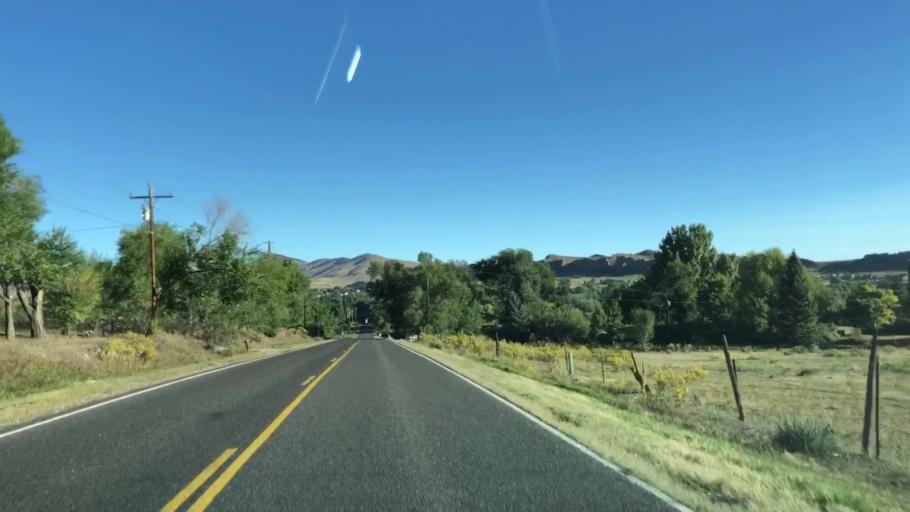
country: US
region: Colorado
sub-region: Larimer County
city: Loveland
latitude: 40.4068
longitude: -105.1688
